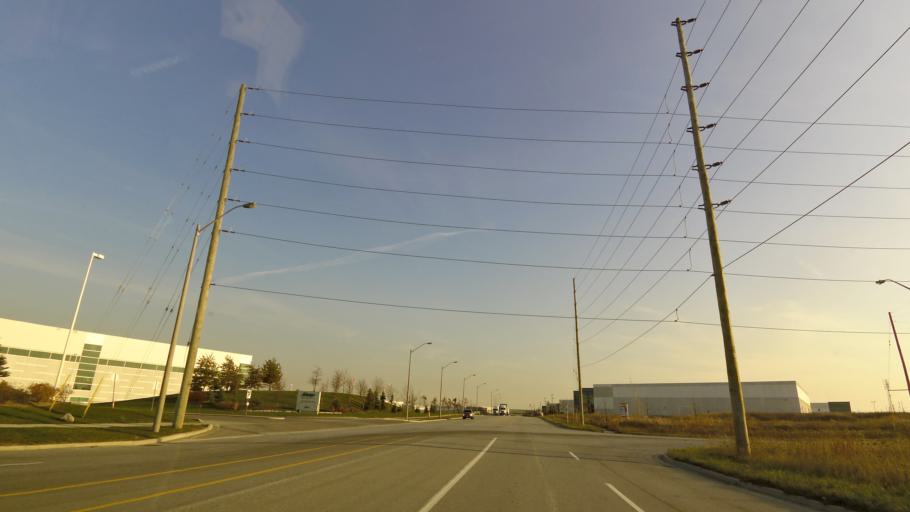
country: CA
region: Ontario
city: Etobicoke
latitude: 43.7805
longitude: -79.6492
